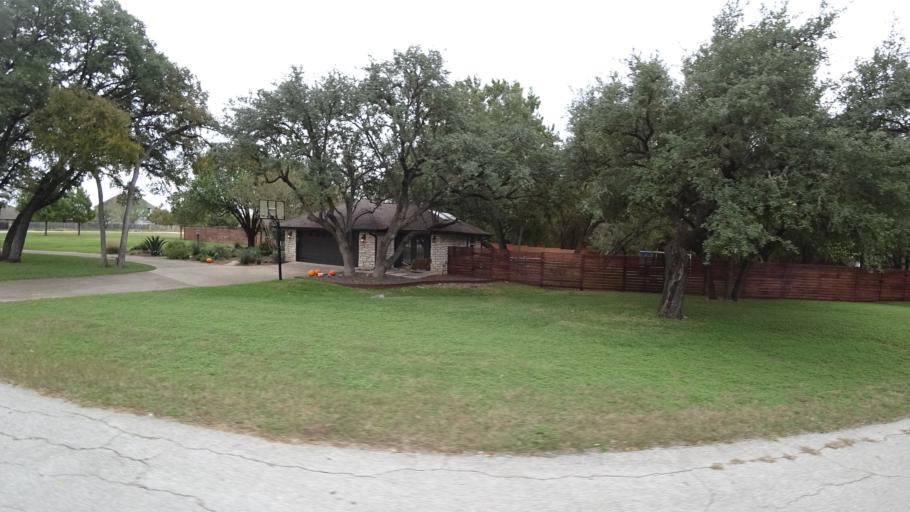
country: US
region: Texas
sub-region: Travis County
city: Shady Hollow
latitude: 30.1521
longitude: -97.8631
